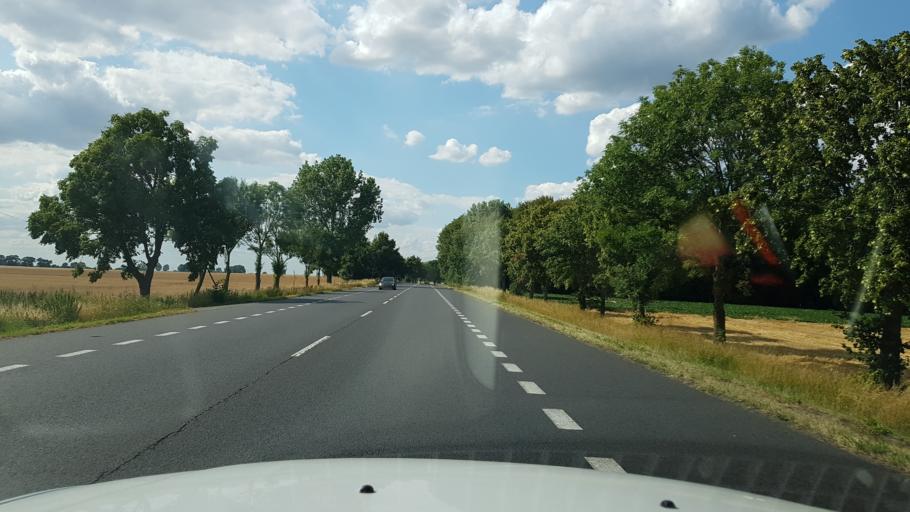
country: PL
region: West Pomeranian Voivodeship
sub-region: Powiat pyrzycki
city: Pyrzyce
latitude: 53.1657
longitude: 14.8625
